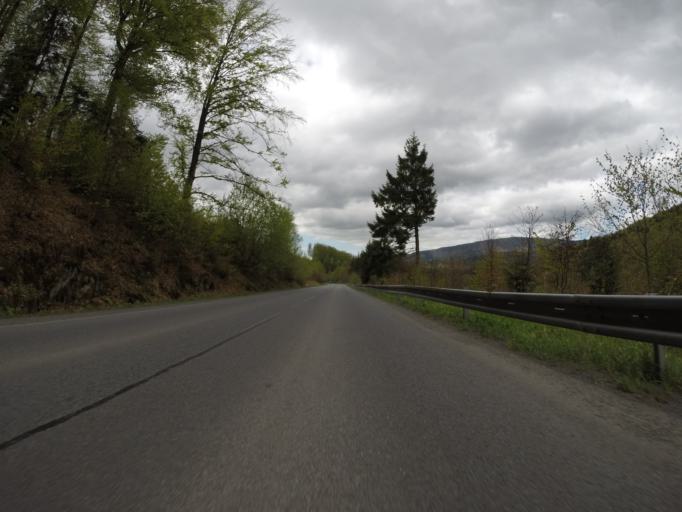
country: SK
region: Banskobystricky
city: Hrinova
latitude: 48.6391
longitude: 19.5862
